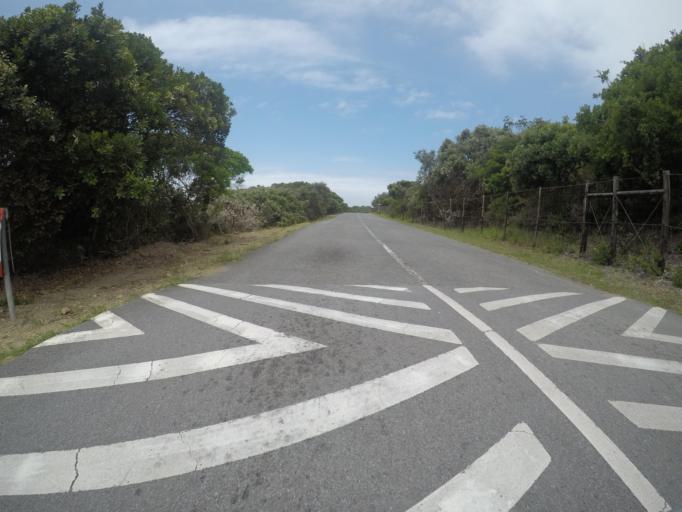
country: ZA
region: Eastern Cape
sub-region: Buffalo City Metropolitan Municipality
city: East London
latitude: -32.9938
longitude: 27.9464
